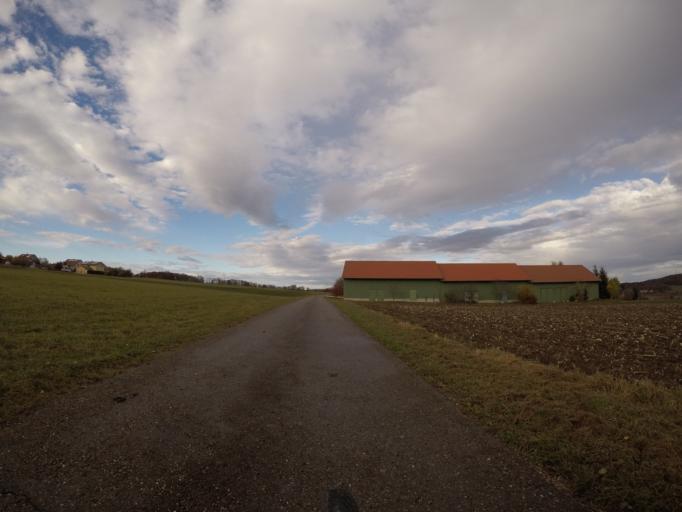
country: DE
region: Baden-Wuerttemberg
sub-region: Tuebingen Region
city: Sankt Johann
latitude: 48.4397
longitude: 9.3254
